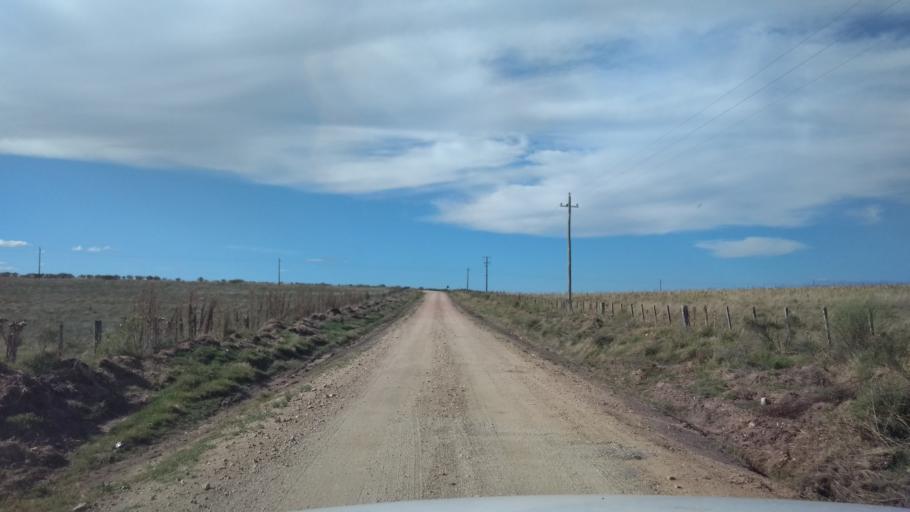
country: UY
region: Florida
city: Casupa
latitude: -34.0030
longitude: -55.7876
